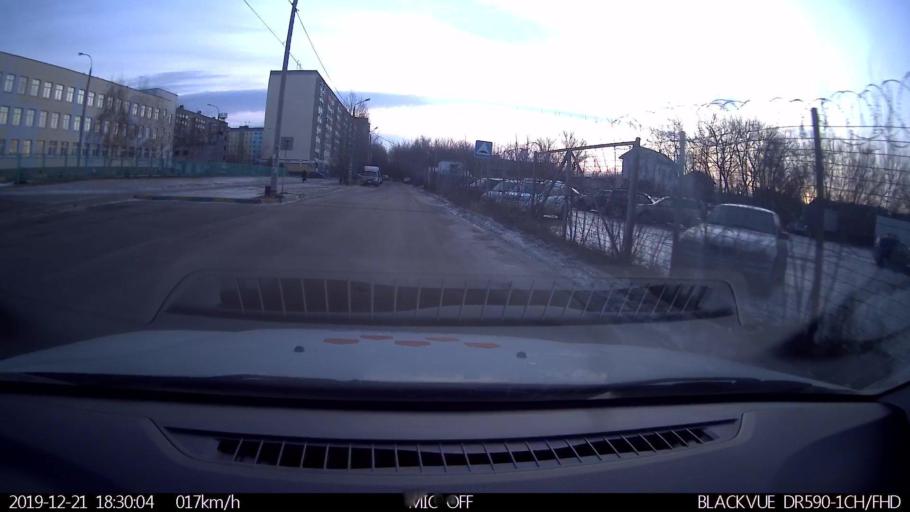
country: RU
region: Nizjnij Novgorod
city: Nizhniy Novgorod
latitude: 56.3362
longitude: 43.9135
